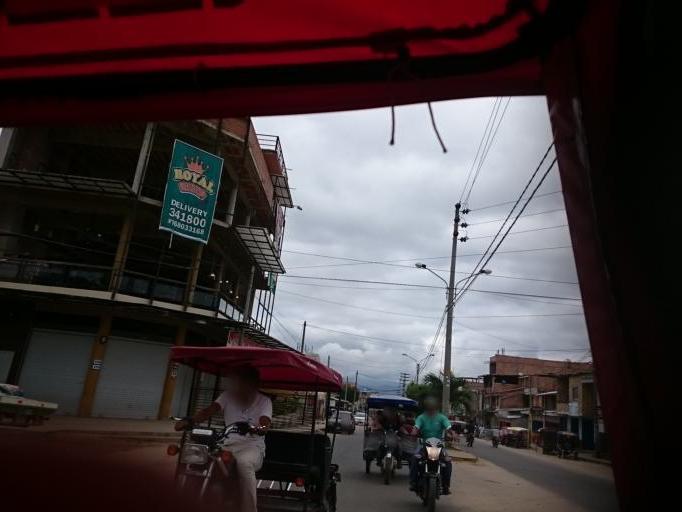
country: PE
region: San Martin
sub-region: Provincia de San Martin
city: Tarapoto
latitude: -6.4913
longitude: -76.3693
